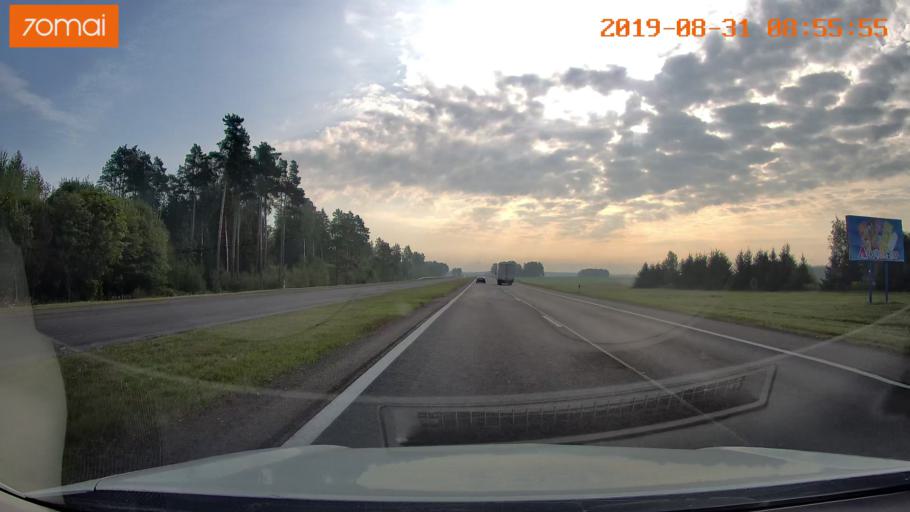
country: BY
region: Minsk
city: Smilavichy
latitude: 53.7646
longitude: 28.1192
